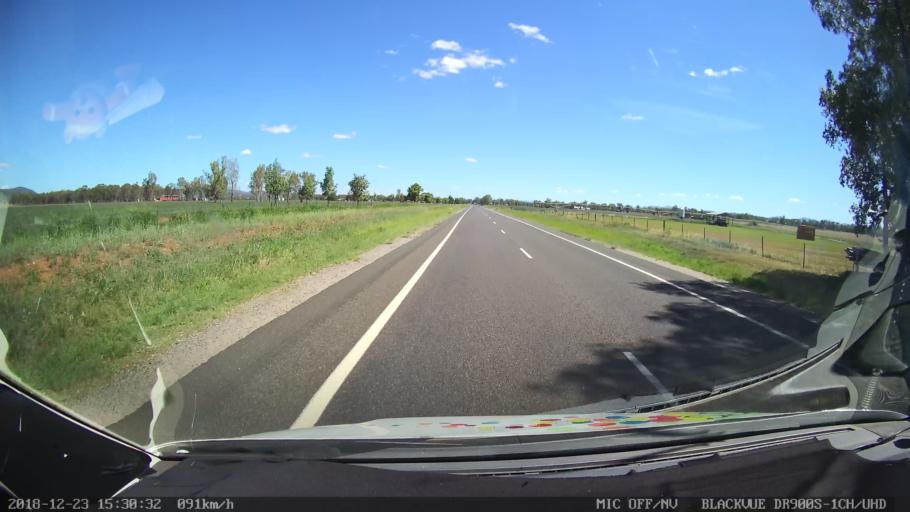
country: AU
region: New South Wales
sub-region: Tamworth Municipality
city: East Tamworth
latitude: -30.9599
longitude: 150.8663
